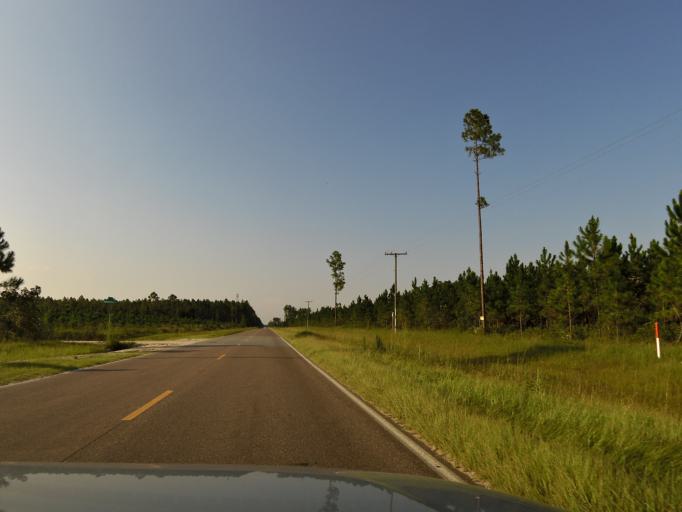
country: US
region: Florida
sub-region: Duval County
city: Baldwin
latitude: 30.3288
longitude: -82.0087
